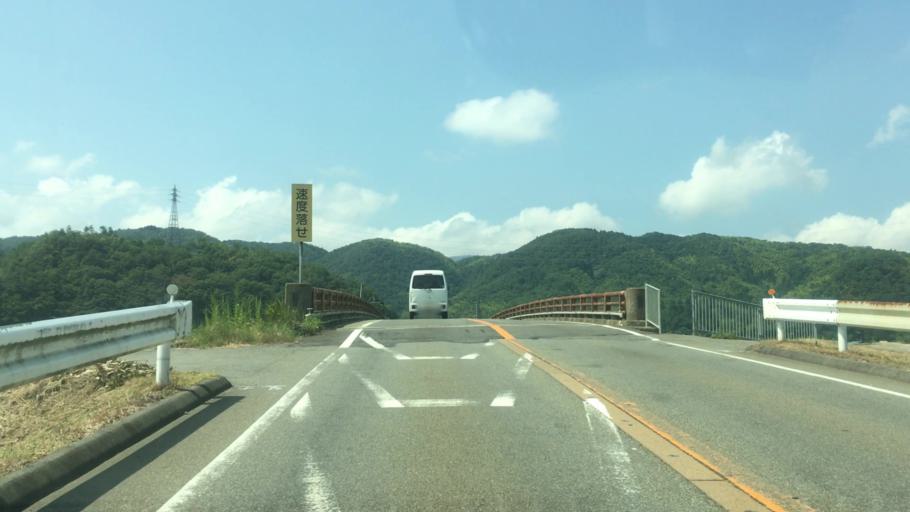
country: JP
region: Hyogo
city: Toyooka
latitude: 35.5583
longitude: 134.7968
